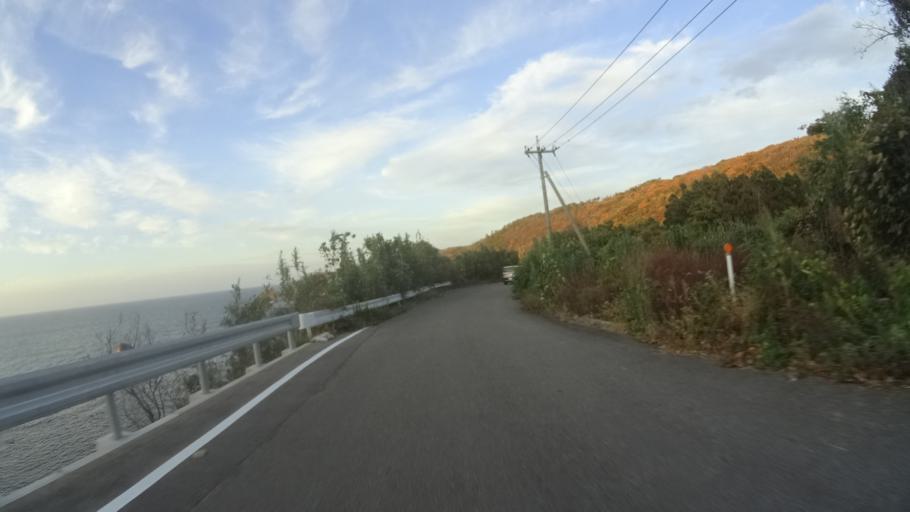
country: JP
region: Ishikawa
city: Nanao
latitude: 37.2145
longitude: 136.6939
